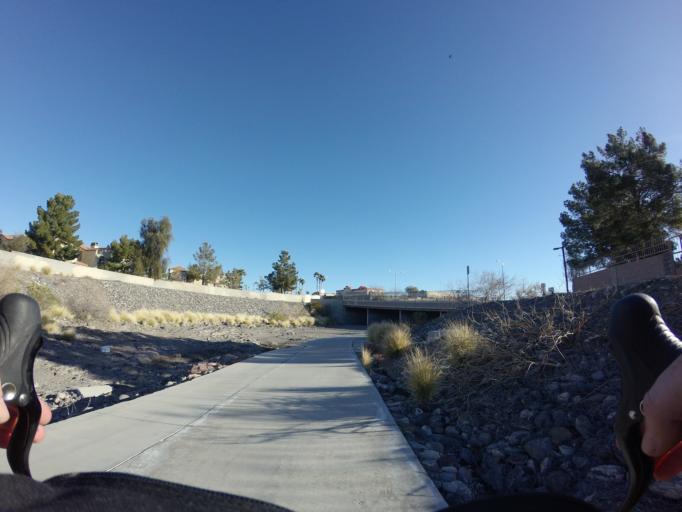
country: US
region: Nevada
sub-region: Clark County
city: Whitney
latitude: 36.0398
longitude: -115.1009
